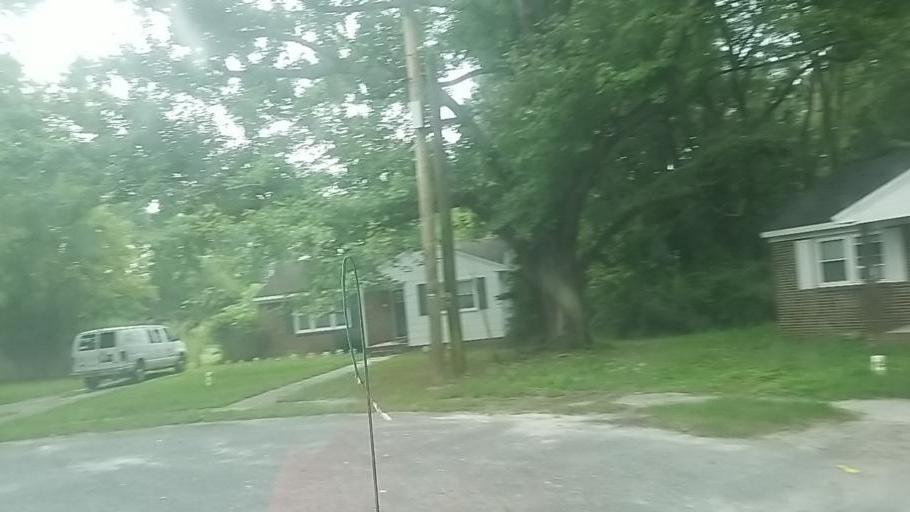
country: US
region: Maryland
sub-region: Wicomico County
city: Salisbury
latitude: 38.3632
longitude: -75.5425
